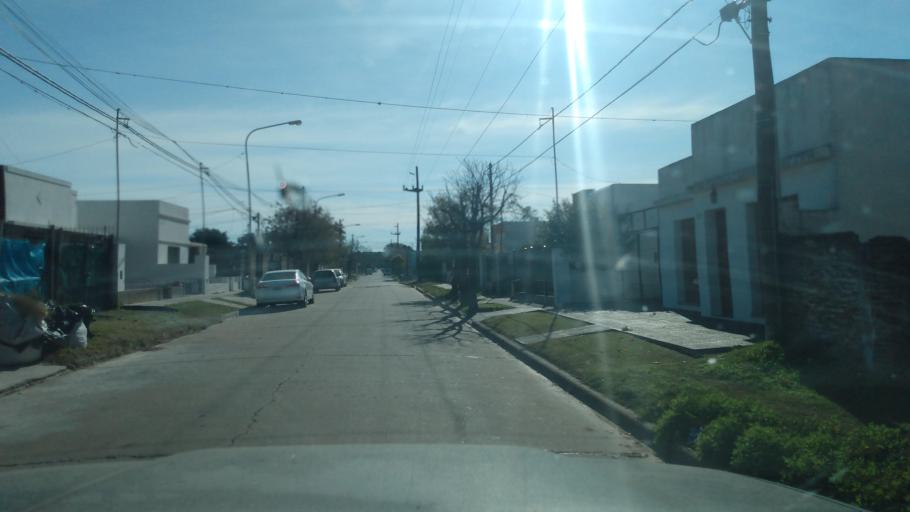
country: AR
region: Buenos Aires
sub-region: Partido de Lujan
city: Lujan
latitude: -34.5684
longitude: -59.1309
